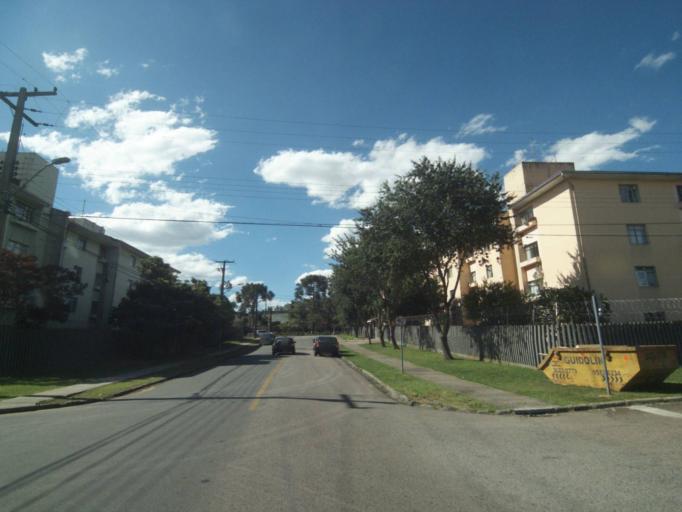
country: BR
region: Parana
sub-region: Curitiba
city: Curitiba
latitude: -25.4963
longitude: -49.3213
